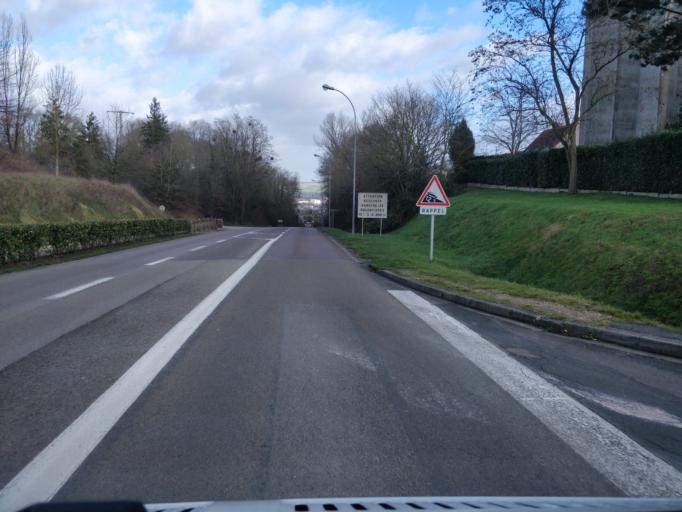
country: FR
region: Bourgogne
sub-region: Departement de l'Yonne
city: Paron
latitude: 48.1907
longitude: 3.2511
